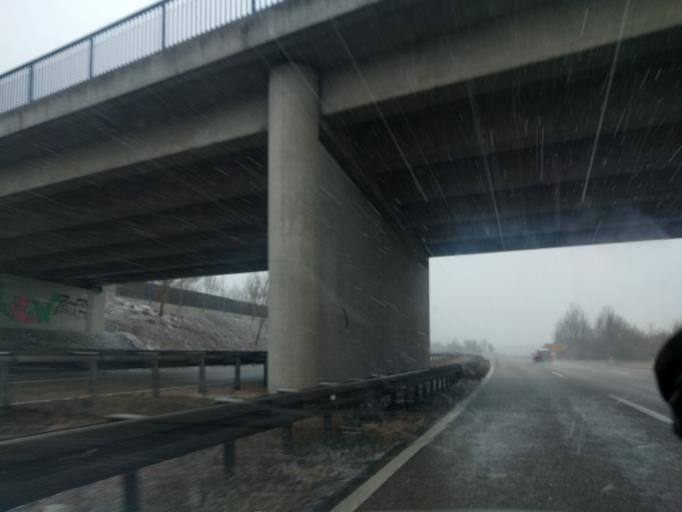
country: DE
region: Bavaria
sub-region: Swabia
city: Westendorf
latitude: 48.5725
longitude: 10.8472
